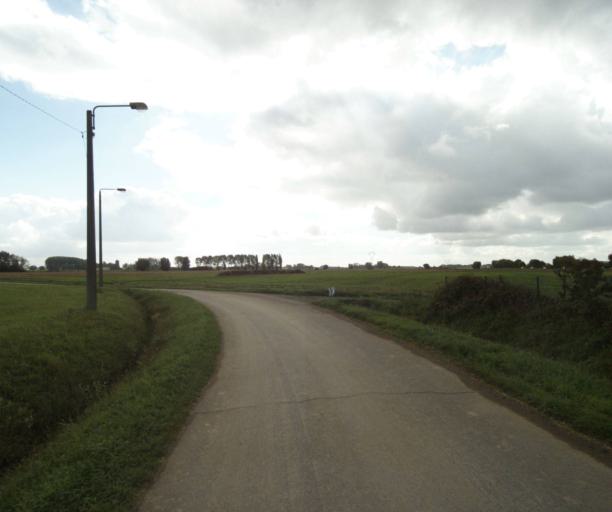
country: FR
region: Nord-Pas-de-Calais
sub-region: Departement du Nord
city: Frelinghien
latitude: 50.7106
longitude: 2.9401
